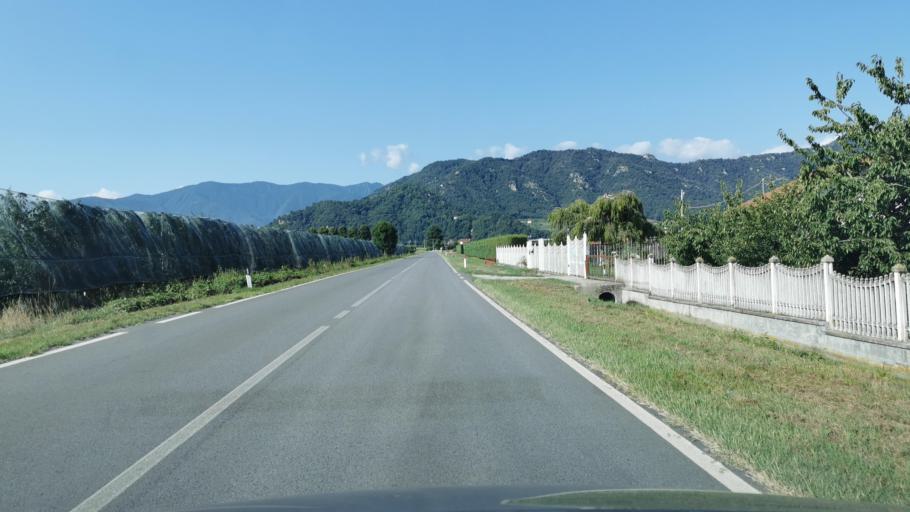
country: IT
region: Piedmont
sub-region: Provincia di Cuneo
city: Revello
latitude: 44.6730
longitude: 7.4033
